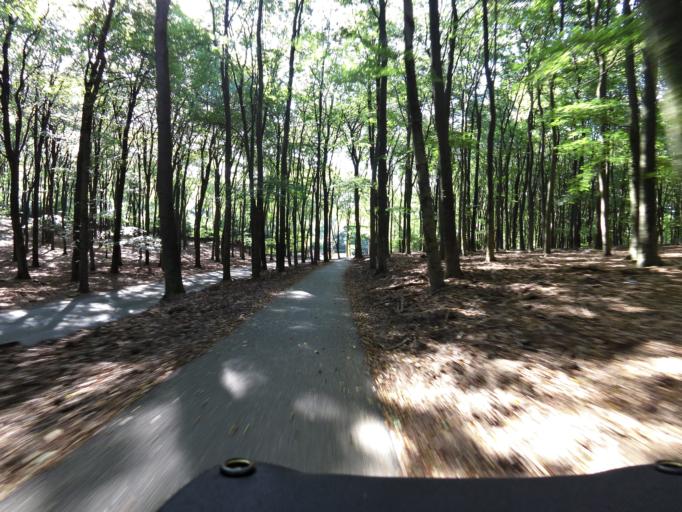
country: NL
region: Gelderland
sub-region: Gemeente Apeldoorn
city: Apeldoorn
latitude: 52.2145
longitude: 5.8736
